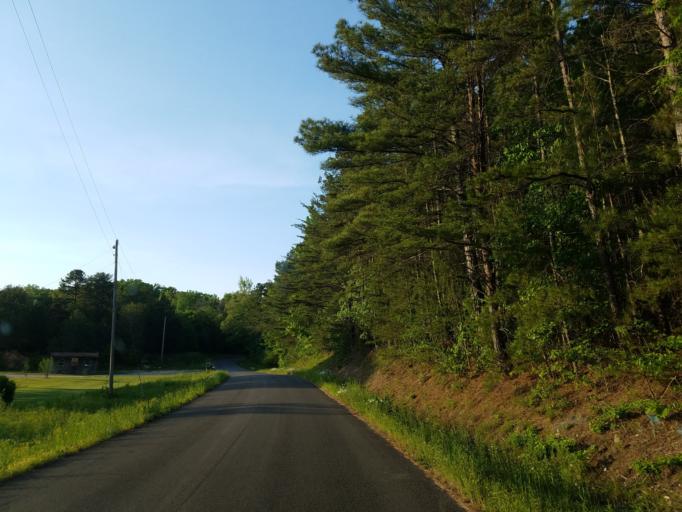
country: US
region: Georgia
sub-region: Whitfield County
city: Dalton
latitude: 34.6546
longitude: -85.0821
